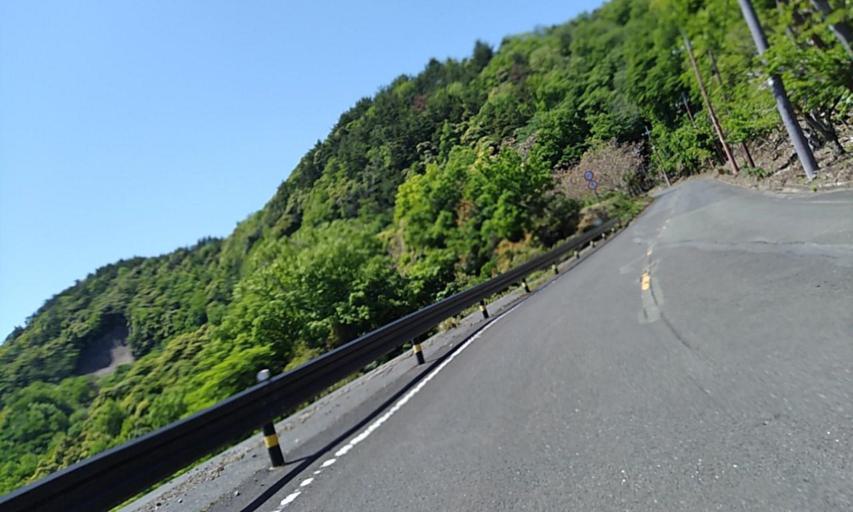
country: JP
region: Fukui
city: Obama
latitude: 35.5453
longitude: 135.7443
